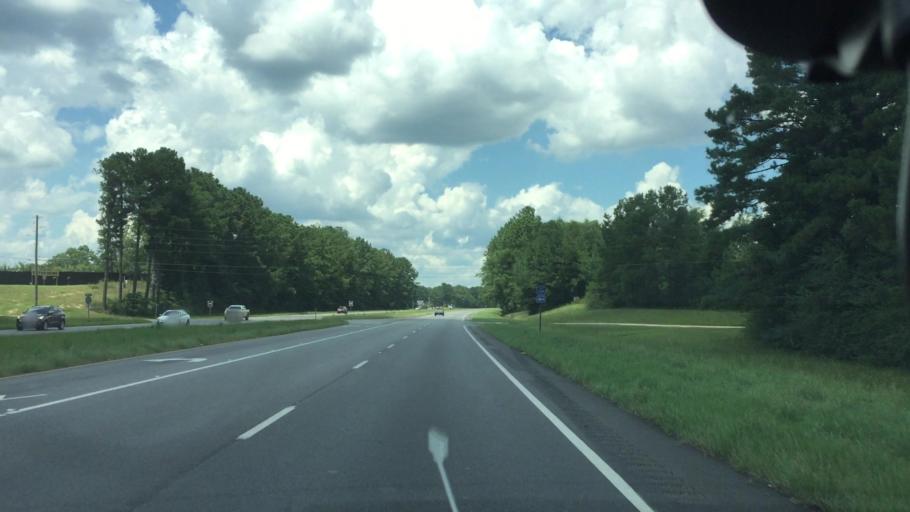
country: US
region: Alabama
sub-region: Pike County
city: Troy
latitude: 31.8899
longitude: -86.0083
